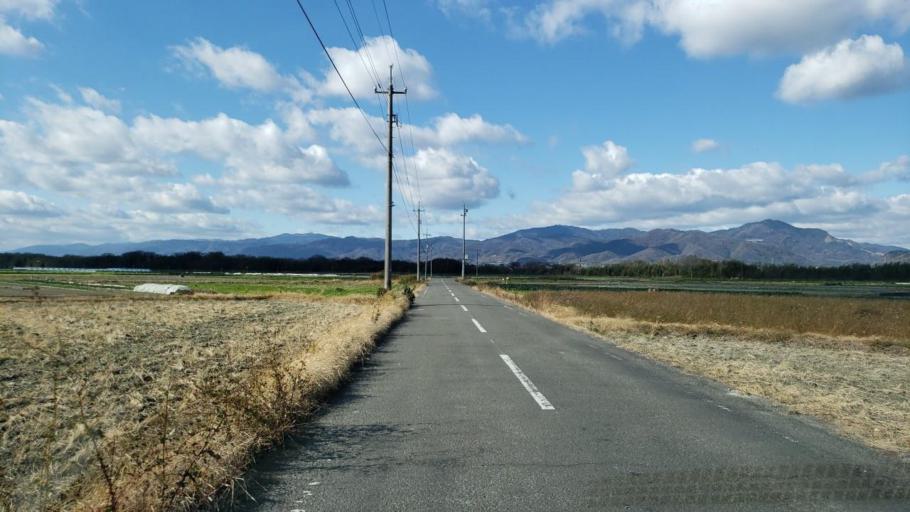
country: JP
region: Tokushima
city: Kamojimacho-jogejima
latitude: 34.0720
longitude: 134.3016
